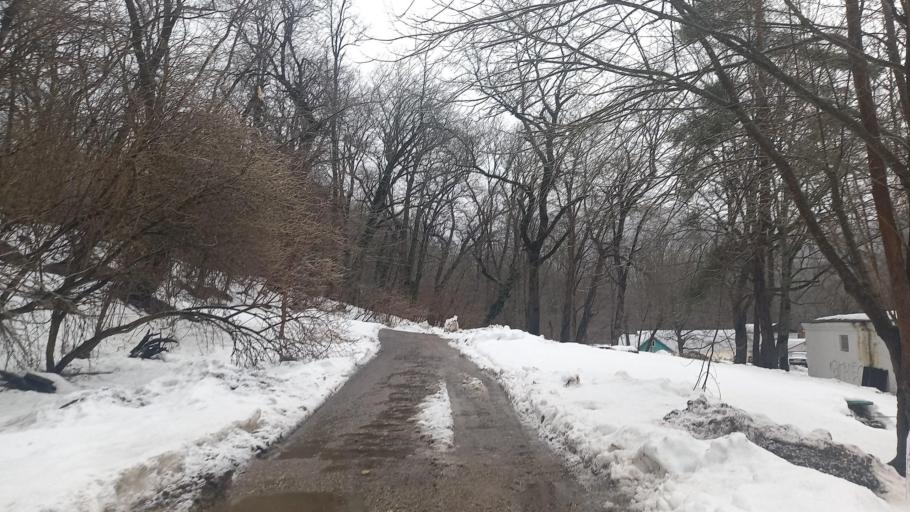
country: RU
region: Krasnodarskiy
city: Goryachiy Klyuch
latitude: 44.6231
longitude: 39.0949
